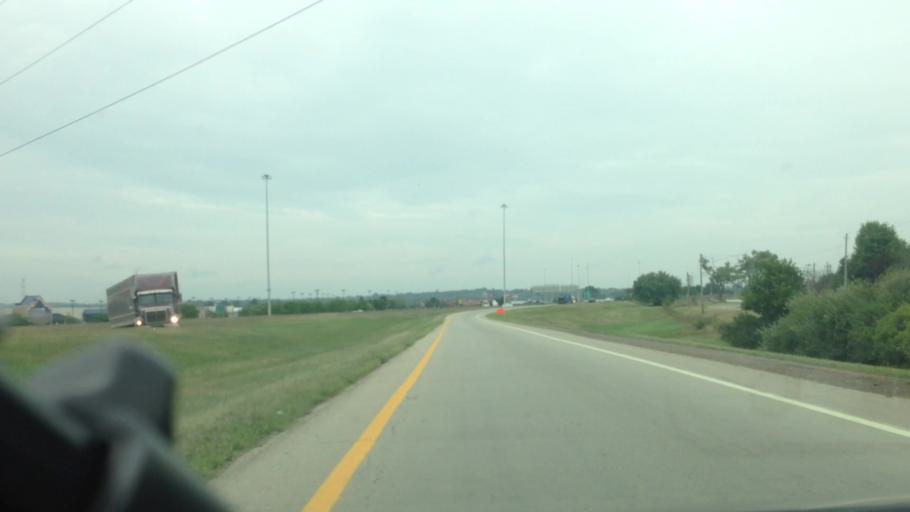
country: US
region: Ohio
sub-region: Stark County
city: Massillon
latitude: 40.7622
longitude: -81.5138
